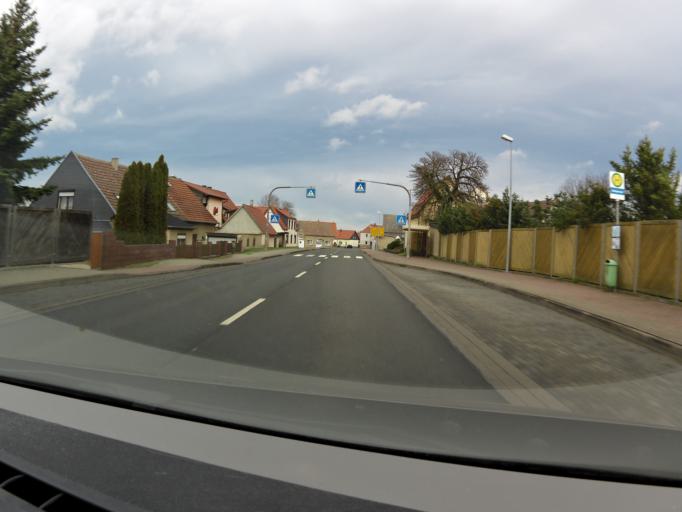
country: DE
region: Saxony-Anhalt
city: Mansfeld
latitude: 51.5633
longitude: 11.4259
